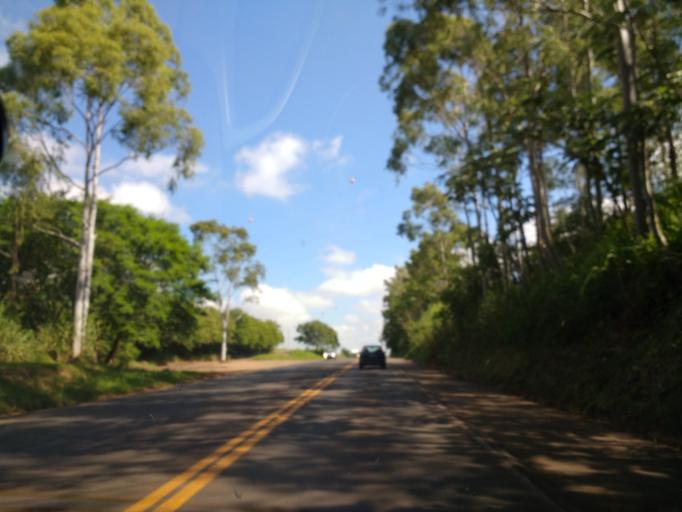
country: BR
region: Parana
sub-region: Umuarama
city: Umuarama
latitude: -23.7698
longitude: -53.2442
